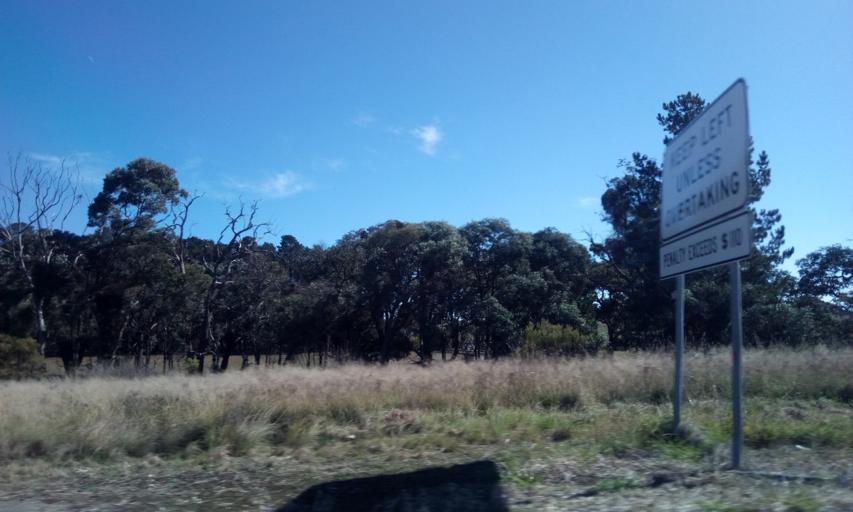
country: AU
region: New South Wales
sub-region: Yass Valley
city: Gundaroo
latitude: -35.1347
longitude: 149.3397
